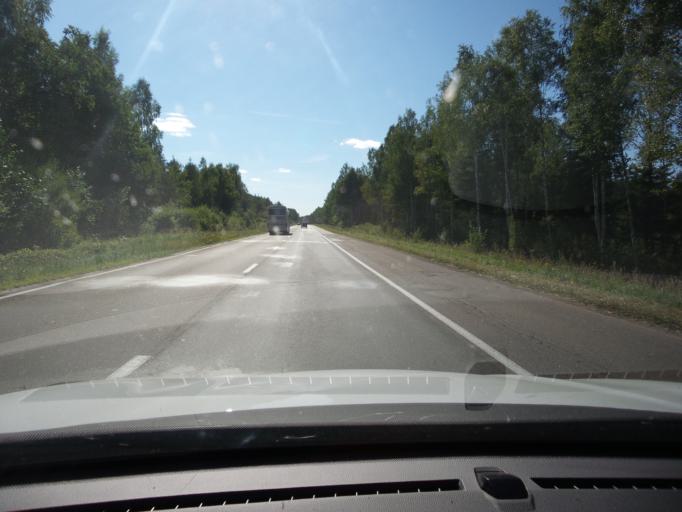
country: LV
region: Seja
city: Loja
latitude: 57.1109
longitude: 24.6171
